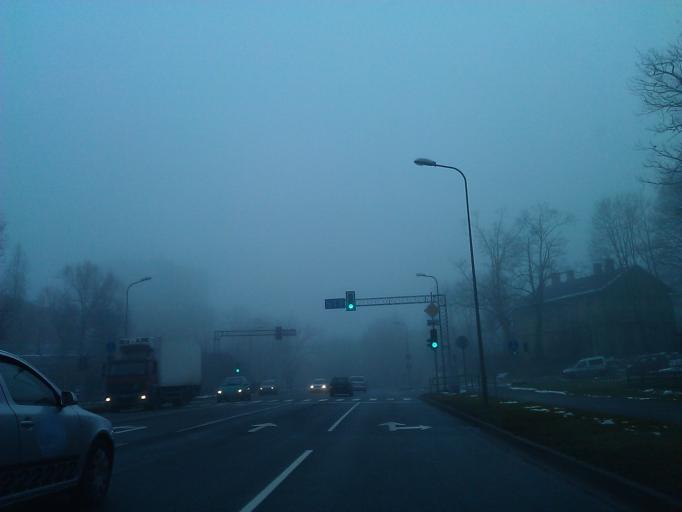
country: LV
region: Riga
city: Bergi
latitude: 56.9867
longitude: 24.2479
